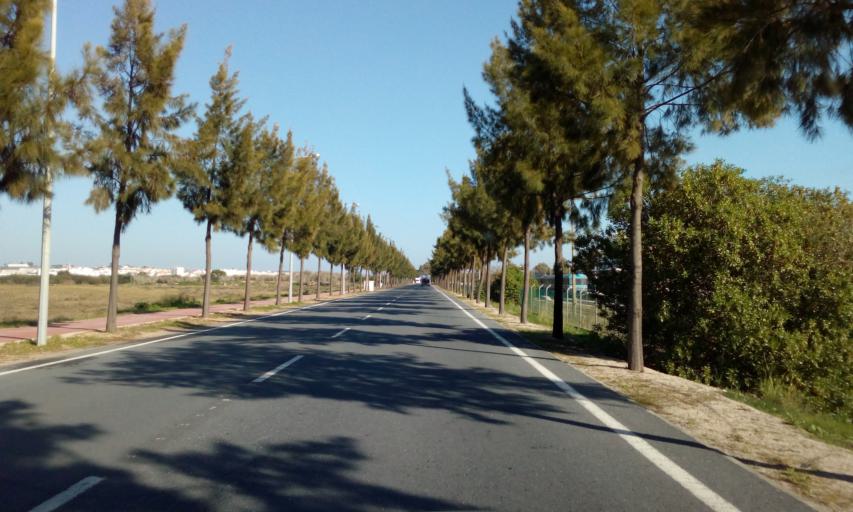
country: PT
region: Faro
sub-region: Vila Real de Santo Antonio
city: Vila Real de Santo Antonio
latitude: 37.1992
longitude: -7.4231
